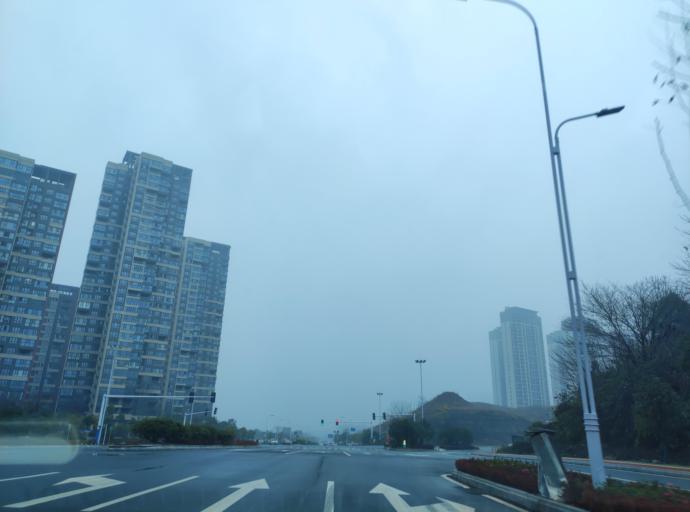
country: CN
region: Jiangxi Sheng
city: Pingxiang
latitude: 27.6672
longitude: 113.8443
